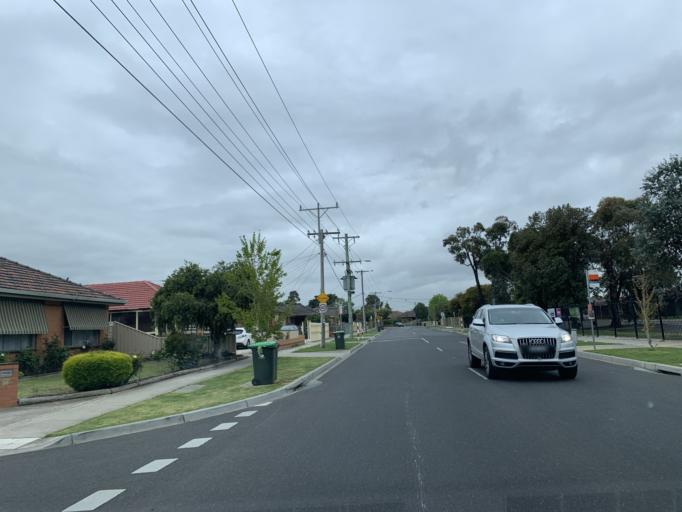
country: AU
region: Victoria
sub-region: Brimbank
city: St Albans
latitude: -37.7561
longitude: 144.8140
